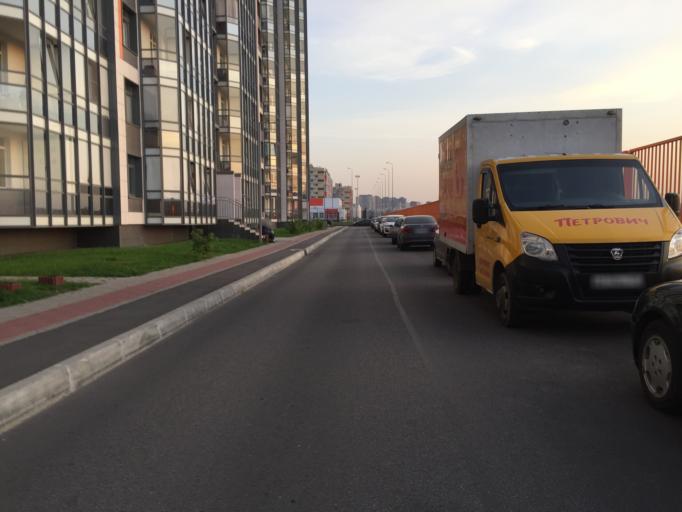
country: RU
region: St.-Petersburg
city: Grazhdanka
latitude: 60.0588
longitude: 30.4152
